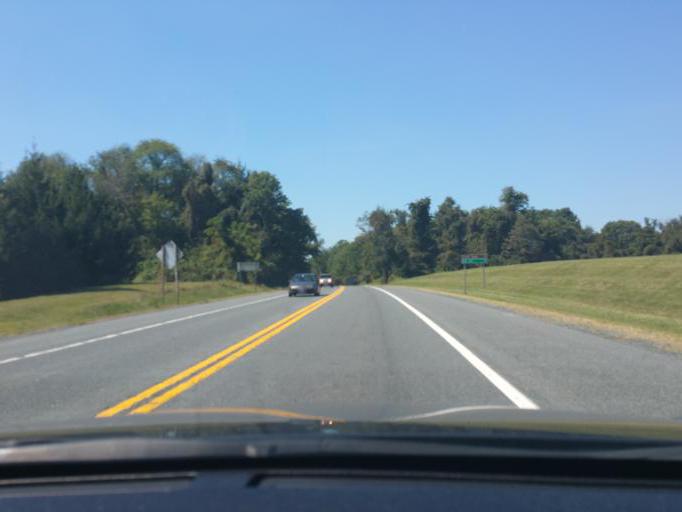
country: US
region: Maryland
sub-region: Harford County
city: Havre de Grace
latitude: 39.5752
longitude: -76.1504
